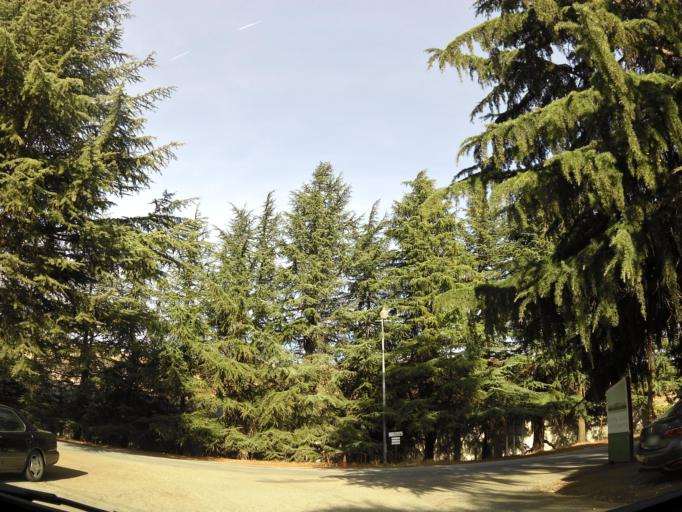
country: US
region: California
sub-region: San Benito County
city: Ridgemark
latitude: 36.7493
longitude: -121.3846
